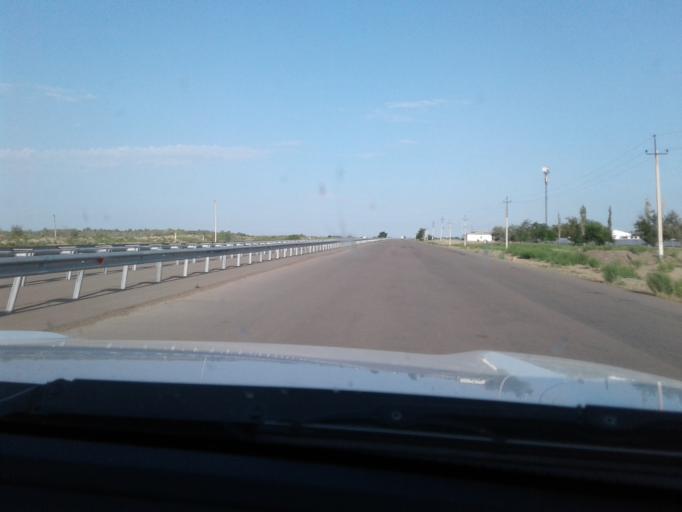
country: TM
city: Akdepe
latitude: 41.7375
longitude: 59.1509
